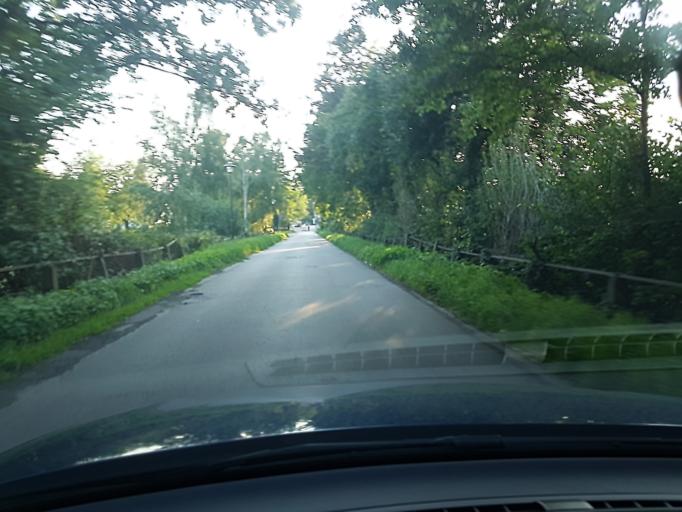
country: DE
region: North Rhine-Westphalia
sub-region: Regierungsbezirk Dusseldorf
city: Ratingen
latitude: 51.3228
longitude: 6.7806
